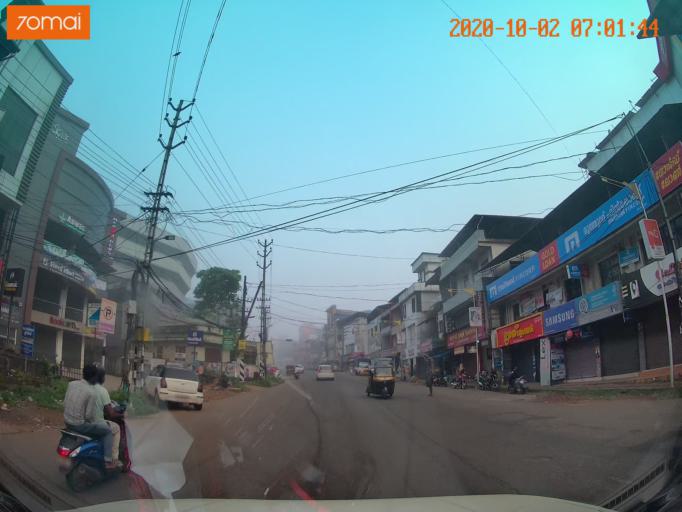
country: IN
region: Kerala
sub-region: Malappuram
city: Malappuram
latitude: 10.8880
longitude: 76.0730
